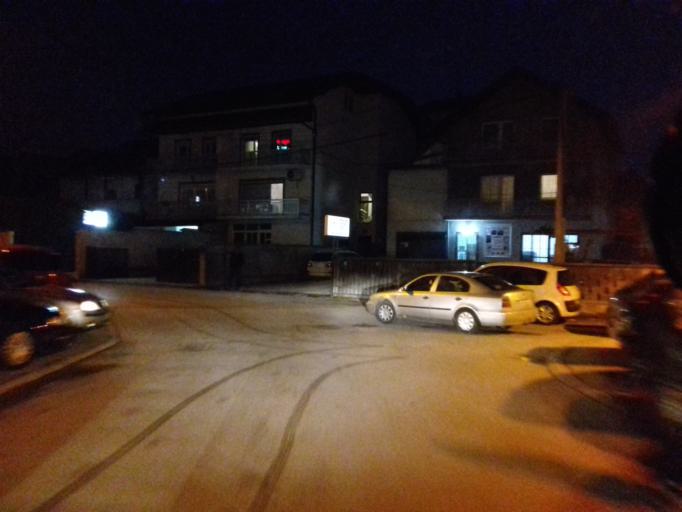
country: BA
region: Federation of Bosnia and Herzegovina
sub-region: Kanton Sarajevo
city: Sarajevo
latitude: 43.8424
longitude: 18.3331
